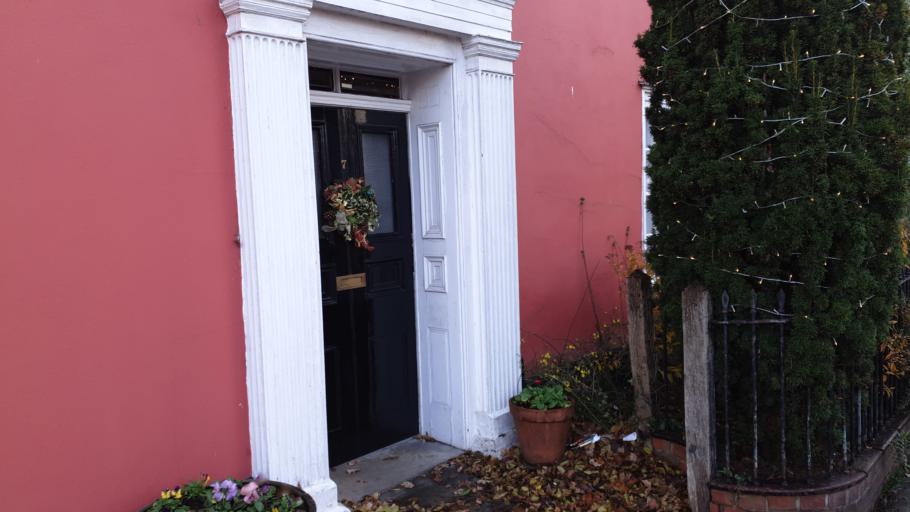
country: GB
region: England
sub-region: Suffolk
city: Hadleigh
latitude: 52.0415
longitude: 0.9555
